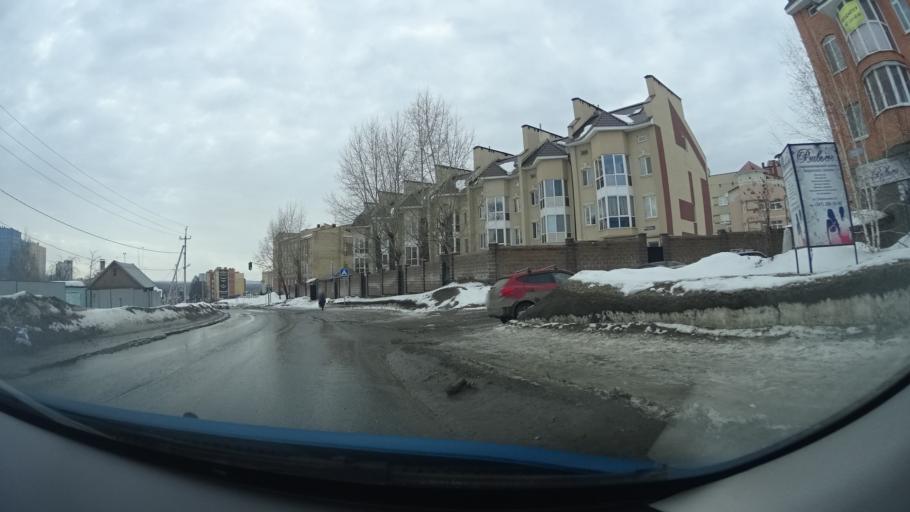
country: RU
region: Bashkortostan
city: Ufa
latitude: 54.6953
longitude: 55.9887
